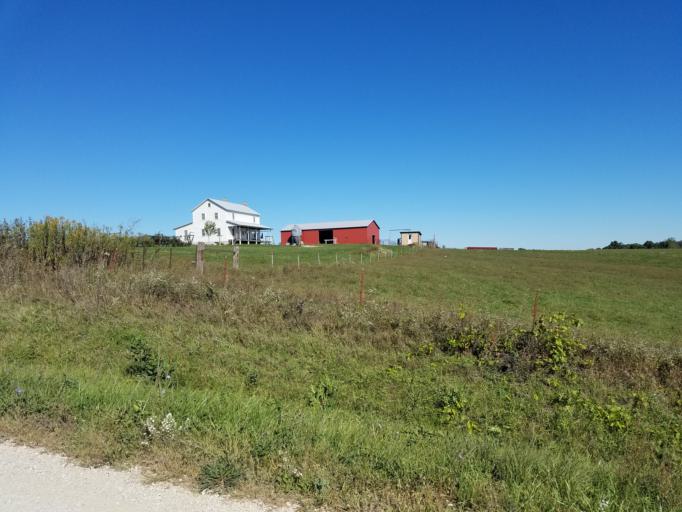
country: US
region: Iowa
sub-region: Decatur County
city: Lamoni
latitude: 40.6093
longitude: -93.8519
